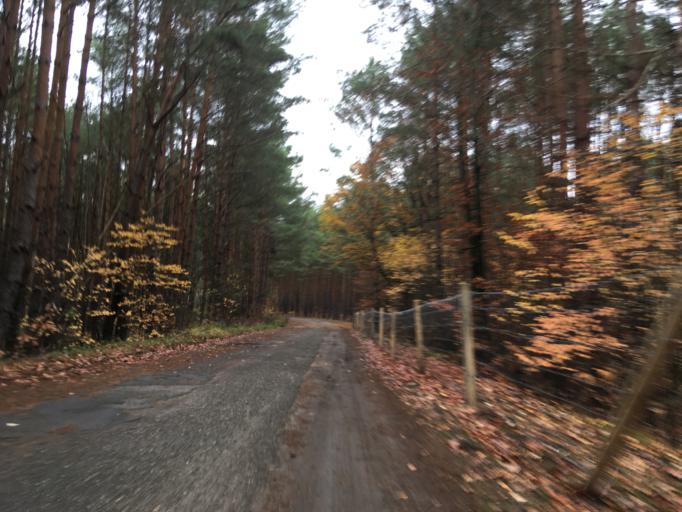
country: DE
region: Brandenburg
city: Jamlitz
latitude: 52.0629
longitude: 14.4823
